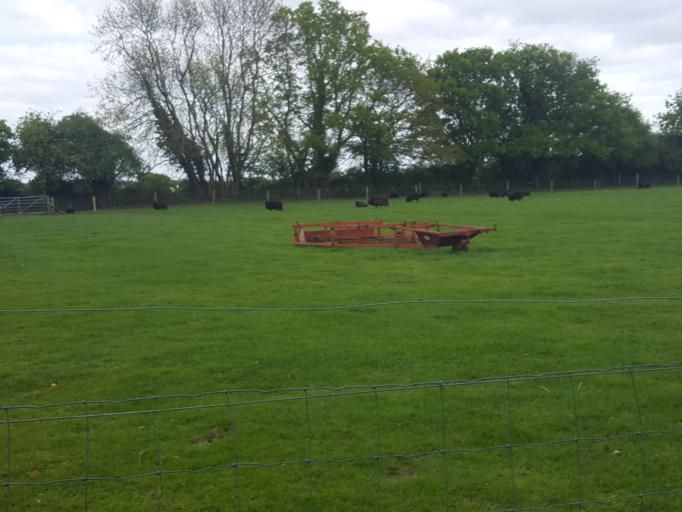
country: GB
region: England
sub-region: Essex
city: Frinton-on-Sea
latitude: 51.8417
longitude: 1.2085
